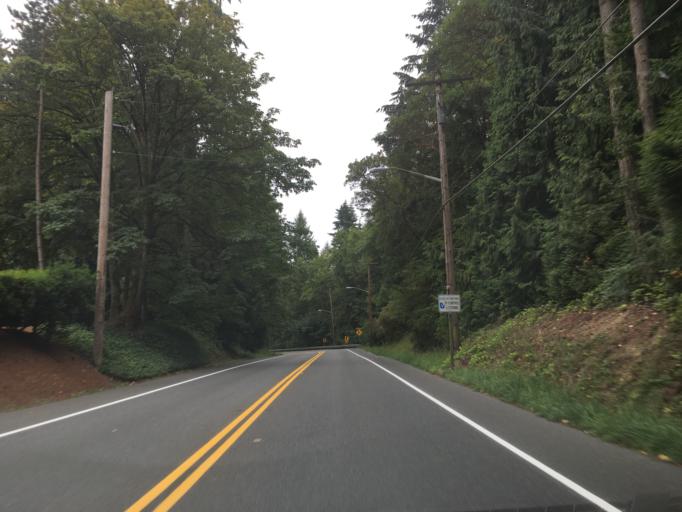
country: US
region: Washington
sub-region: King County
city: Inglewood-Finn Hill
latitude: 47.7267
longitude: -122.2437
